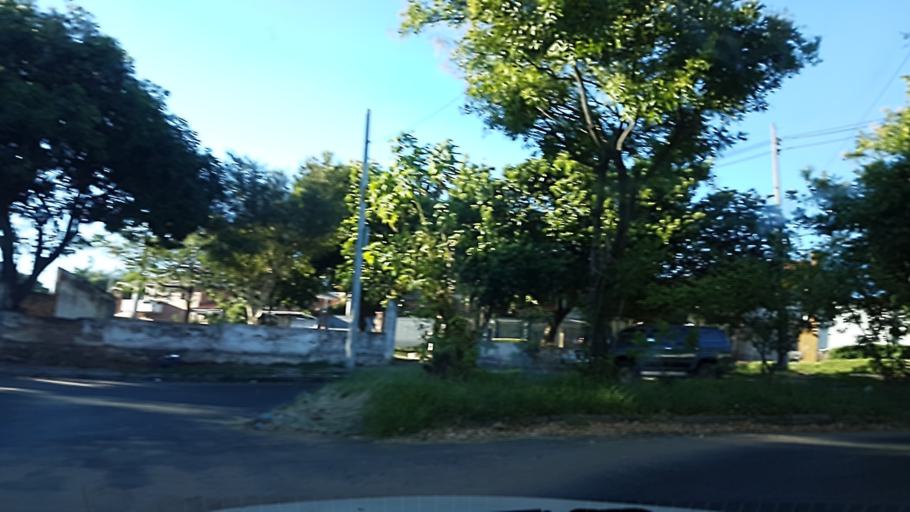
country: PY
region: Asuncion
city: Asuncion
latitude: -25.2727
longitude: -57.5757
